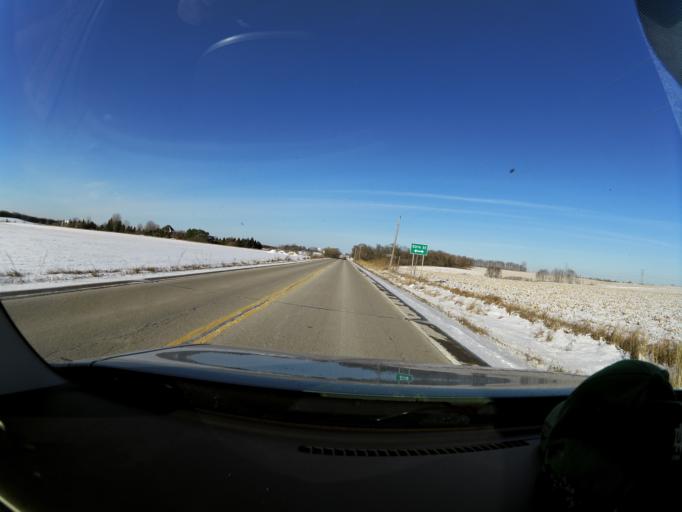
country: US
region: Minnesota
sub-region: Washington County
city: Afton
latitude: 44.8747
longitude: -92.8625
